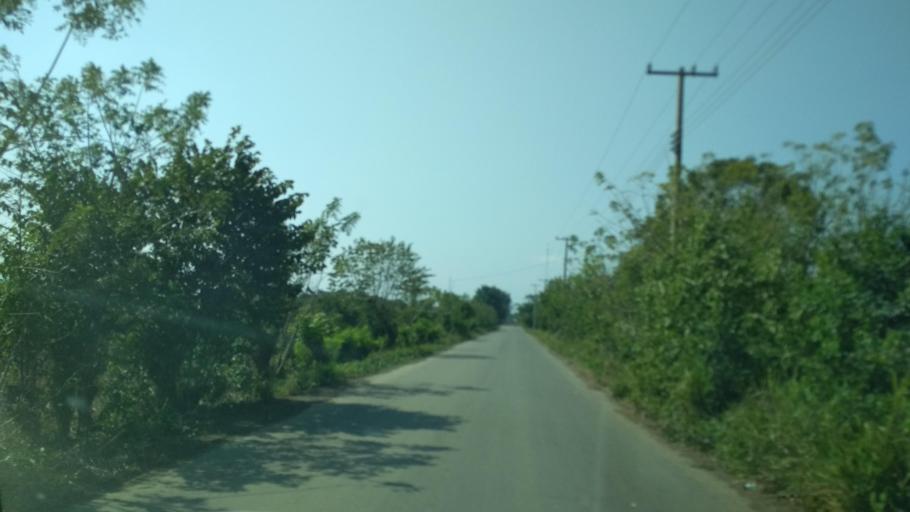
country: MX
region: Puebla
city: San Jose Acateno
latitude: 20.1989
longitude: -97.1835
